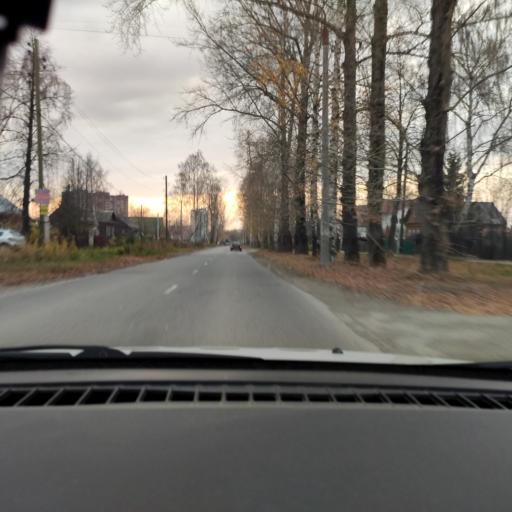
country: RU
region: Perm
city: Polazna
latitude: 58.1233
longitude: 56.4018
